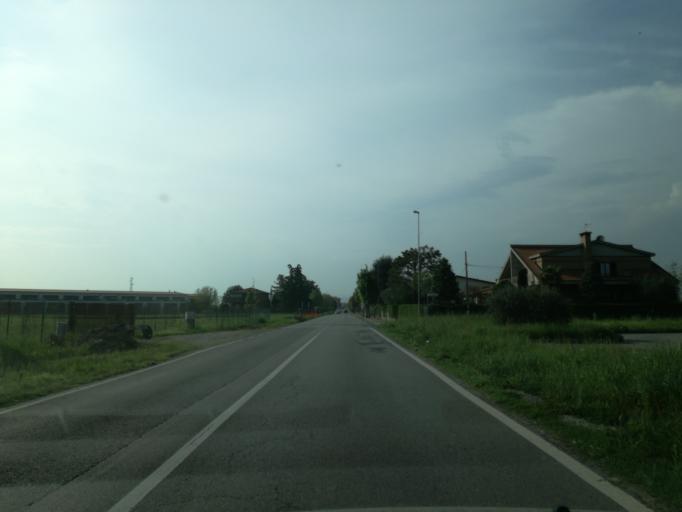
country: IT
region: Lombardy
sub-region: Provincia di Lecco
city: Verderio Superiore
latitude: 45.6605
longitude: 9.4520
